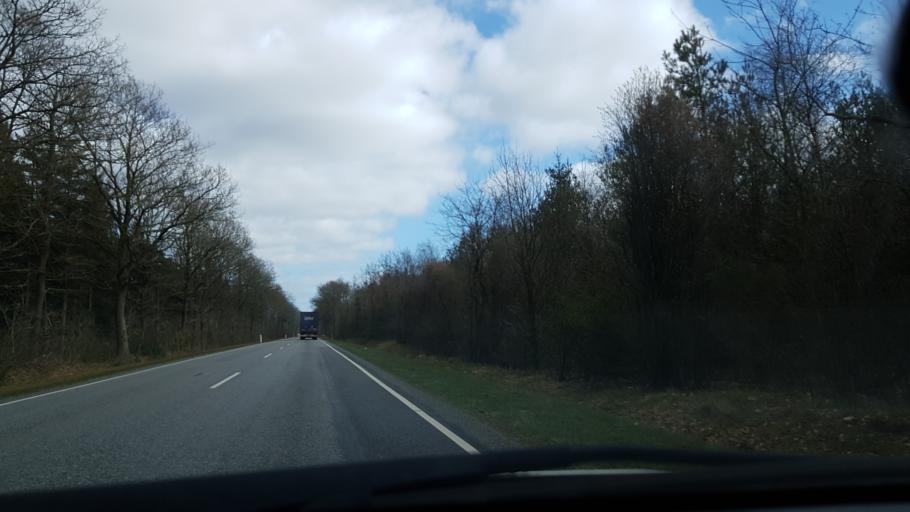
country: DK
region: South Denmark
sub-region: Esbjerg Kommune
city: Ribe
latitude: 55.3001
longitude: 8.8984
